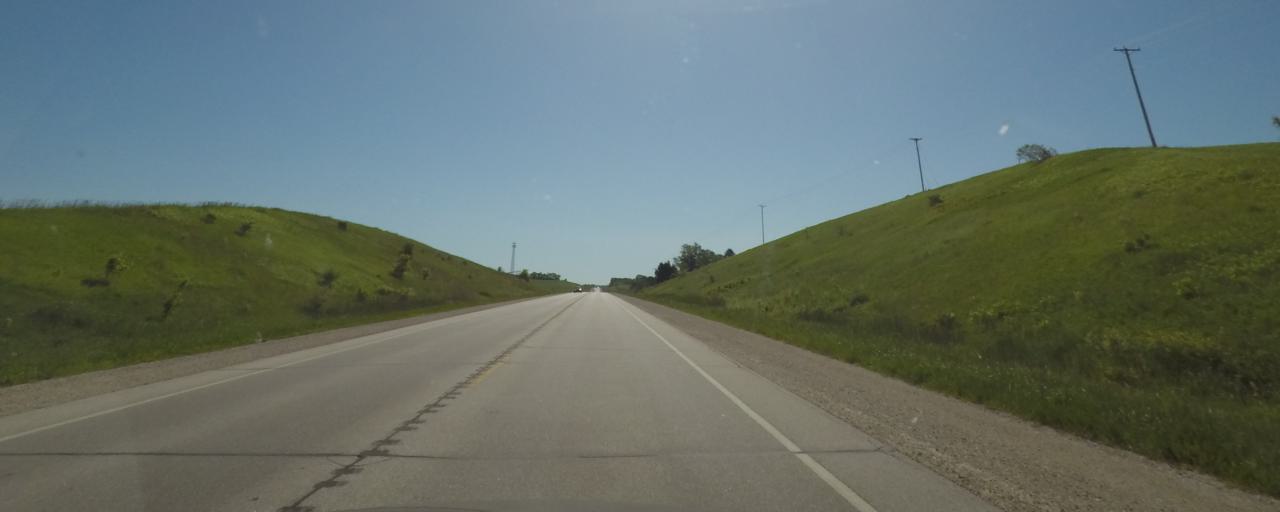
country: US
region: Wisconsin
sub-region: Fond du Lac County
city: Saint Peter
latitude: 43.7832
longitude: -88.3159
